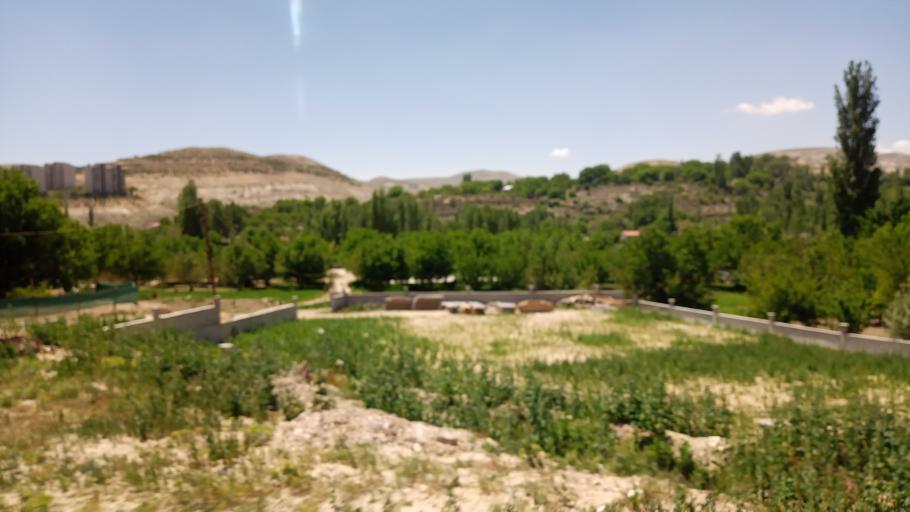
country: TR
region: Sivas
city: Gurun
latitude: 38.7235
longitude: 37.2860
